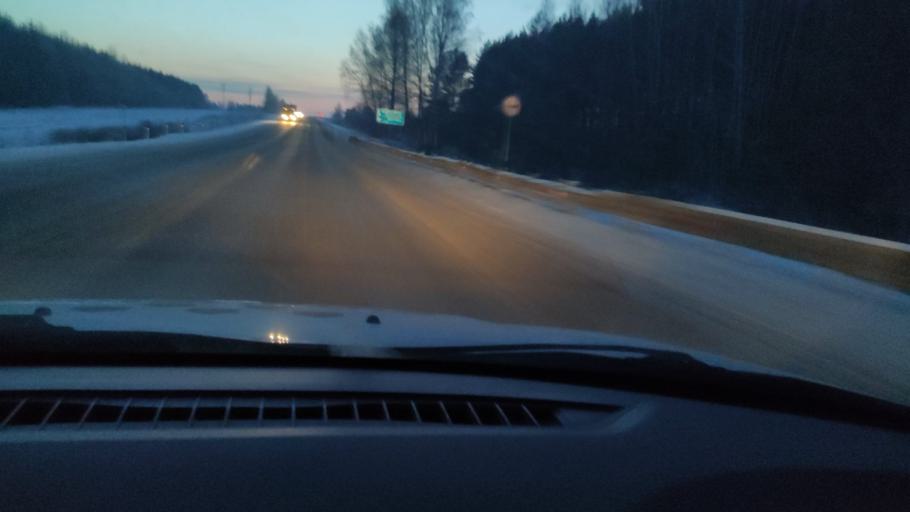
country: RU
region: Perm
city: Kungur
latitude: 57.4085
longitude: 56.9024
